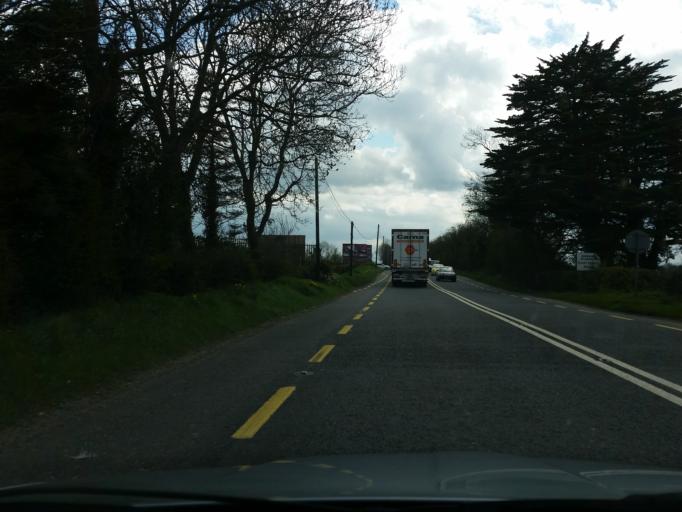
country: IE
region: Leinster
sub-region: An Mhi
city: Ratoath
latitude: 53.5508
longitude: -6.4346
